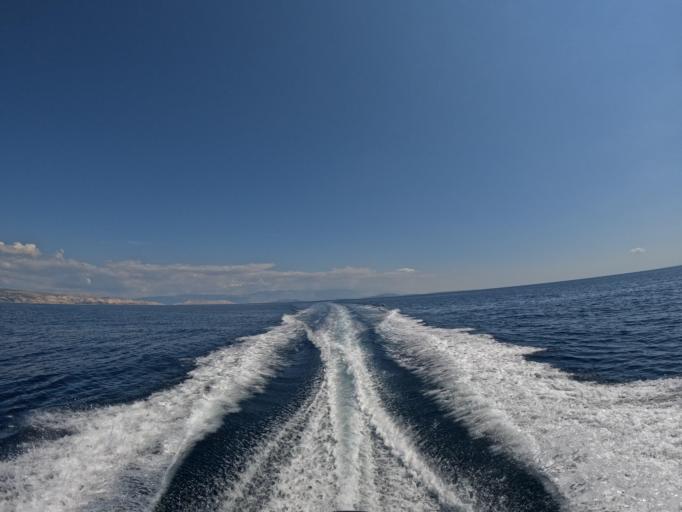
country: HR
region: Primorsko-Goranska
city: Cres
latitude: 44.9333
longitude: 14.5166
